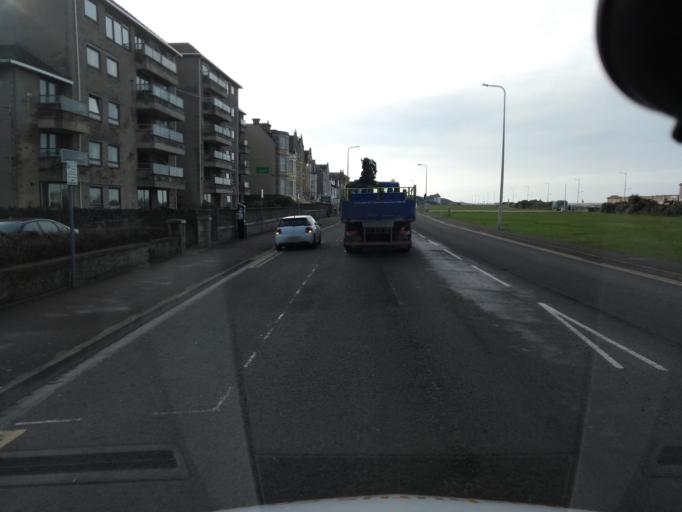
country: GB
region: England
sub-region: North Somerset
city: Weston-super-Mare
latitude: 51.3418
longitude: -2.9807
